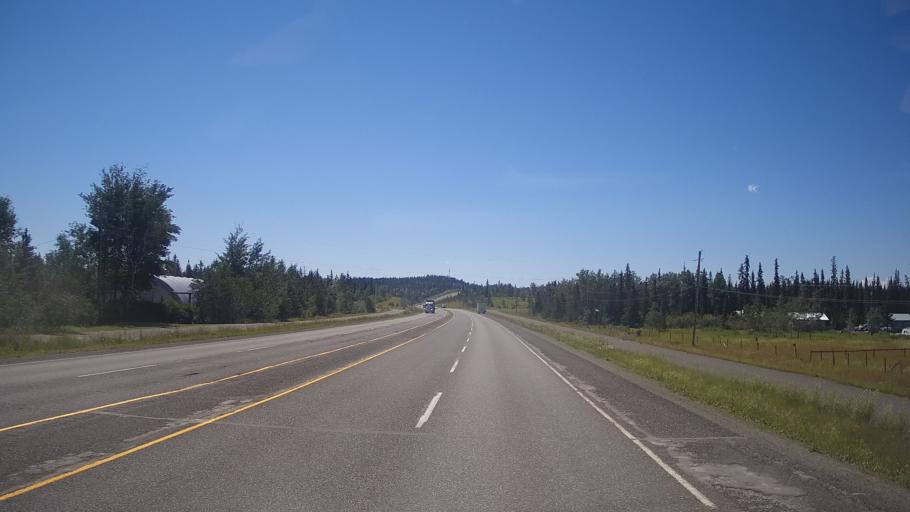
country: CA
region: British Columbia
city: Cache Creek
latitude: 51.5013
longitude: -121.3704
